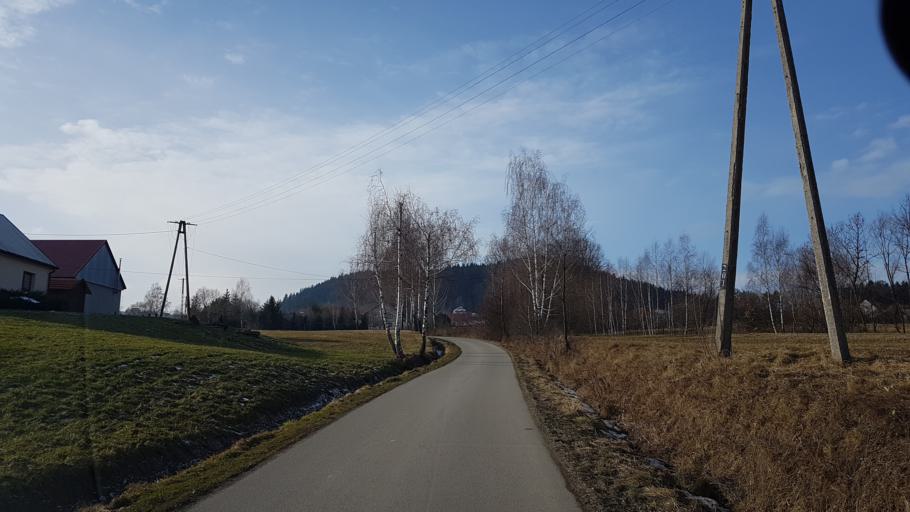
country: PL
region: Lesser Poland Voivodeship
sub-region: Powiat limanowski
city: Lukowica
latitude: 49.6597
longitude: 20.4753
